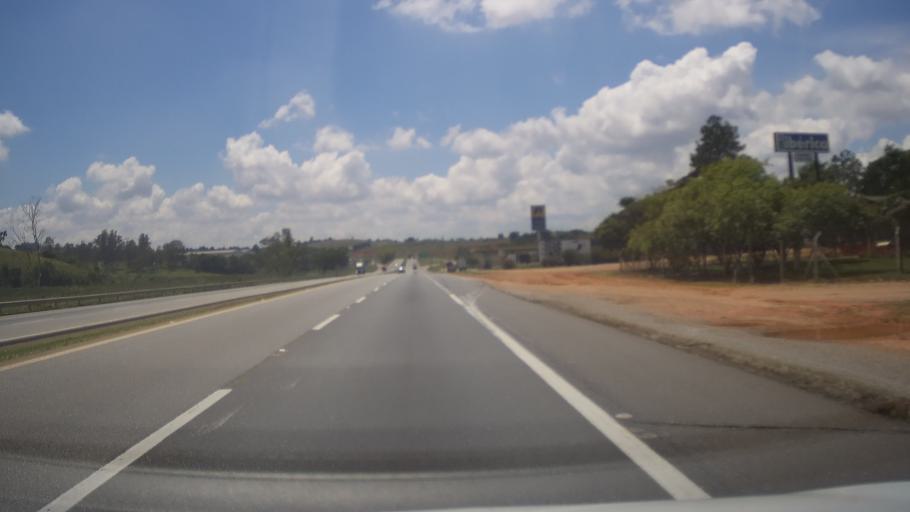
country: BR
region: Minas Gerais
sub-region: Sao Goncalo Do Sapucai
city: Sao Goncalo do Sapucai
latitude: -21.9164
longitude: -45.5863
